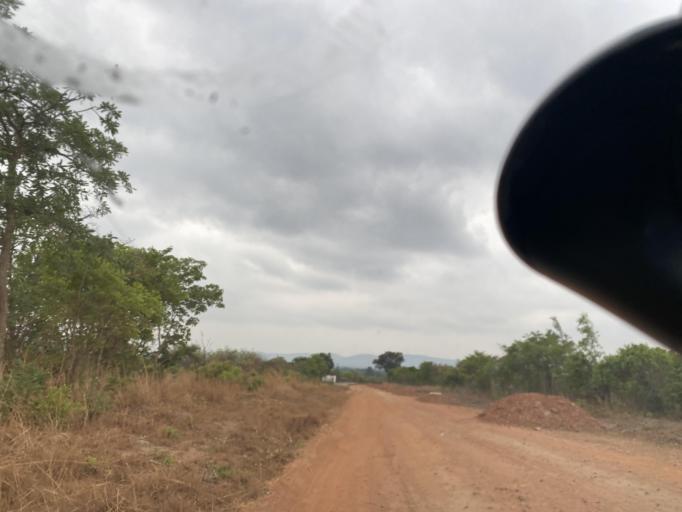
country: ZM
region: Lusaka
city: Chongwe
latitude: -15.2557
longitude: 28.7289
